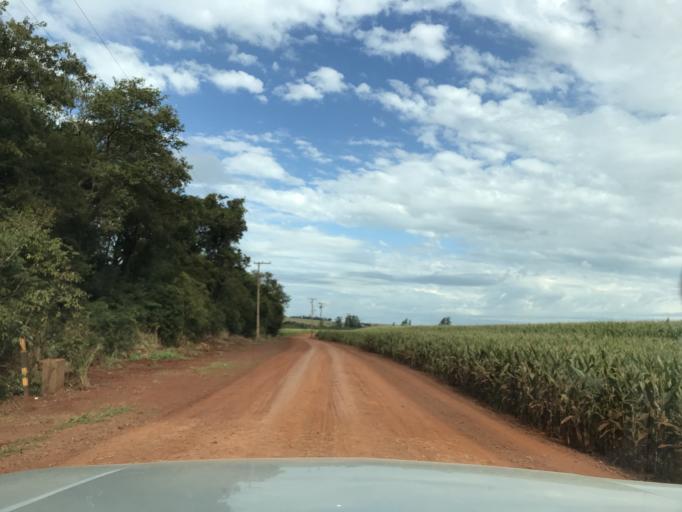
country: BR
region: Parana
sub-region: Palotina
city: Palotina
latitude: -24.3140
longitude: -53.8075
